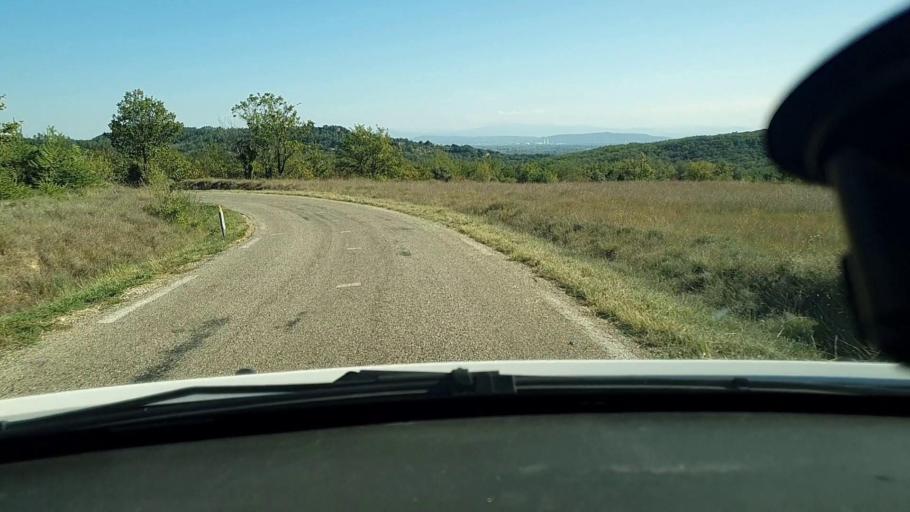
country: FR
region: Languedoc-Roussillon
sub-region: Departement du Gard
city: Saint-Julien-de-Peyrolas
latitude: 44.2692
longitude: 4.5344
